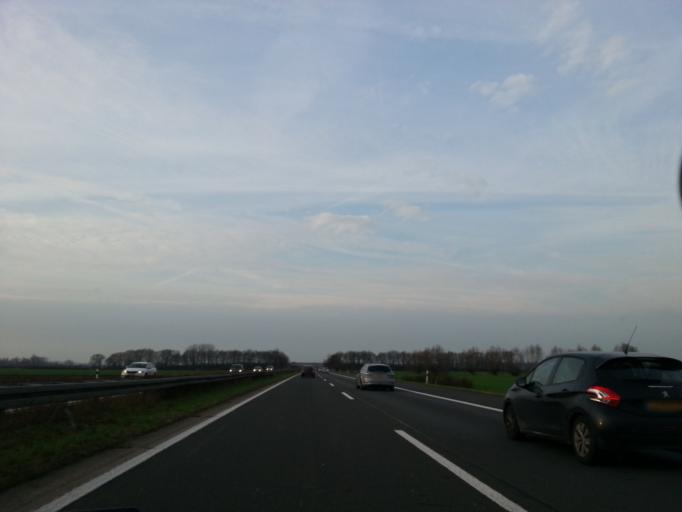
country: NL
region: Gelderland
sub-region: Gemeente Montferland
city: s-Heerenberg
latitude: 51.8510
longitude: 6.2928
